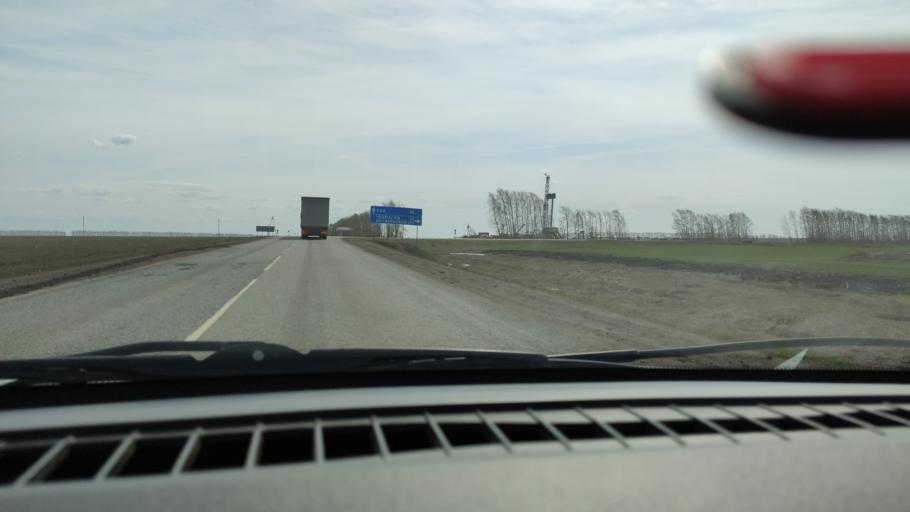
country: RU
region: Bashkortostan
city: Dyurtyuli
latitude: 55.3782
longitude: 54.8684
